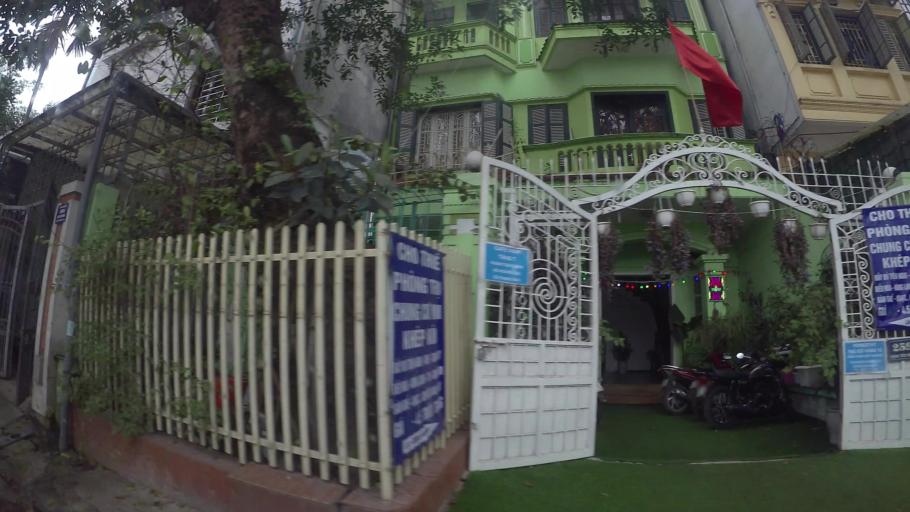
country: VN
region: Ha Noi
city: Dong Da
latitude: 21.0170
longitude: 105.8185
